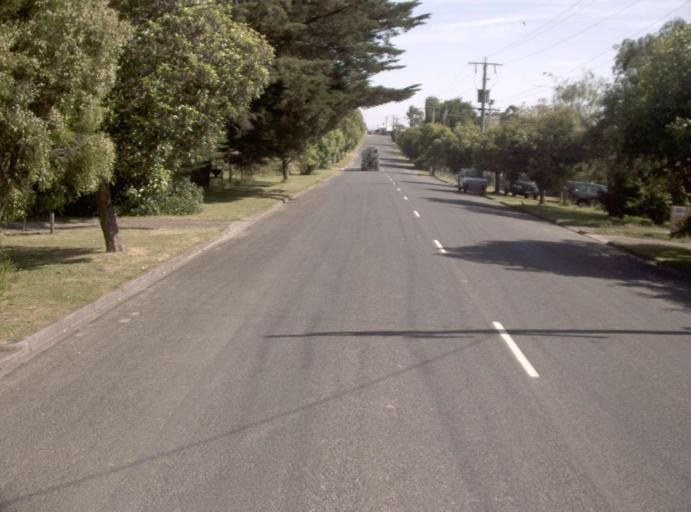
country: AU
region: Victoria
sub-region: Baw Baw
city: Warragul
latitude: -38.3390
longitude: 145.7656
